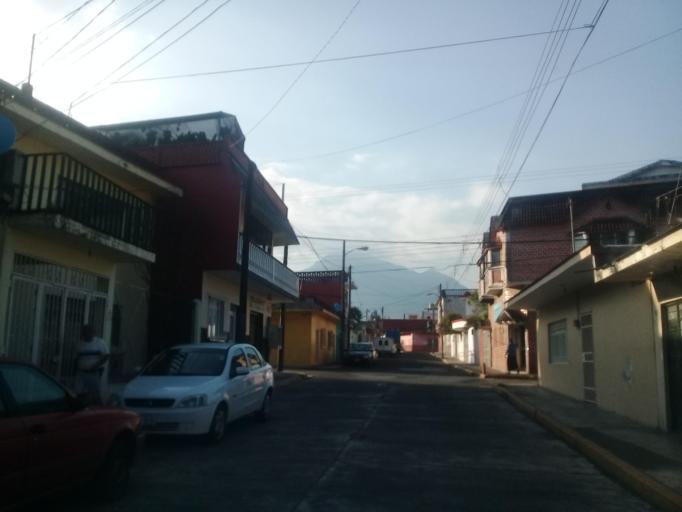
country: MX
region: Veracruz
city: Orizaba
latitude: 18.8553
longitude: -97.1104
